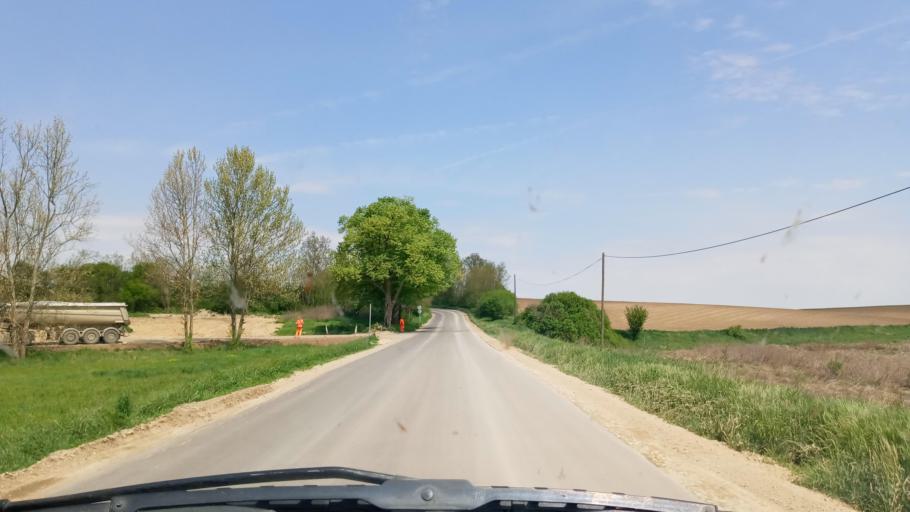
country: HU
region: Baranya
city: Boly
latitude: 45.9230
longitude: 18.5457
